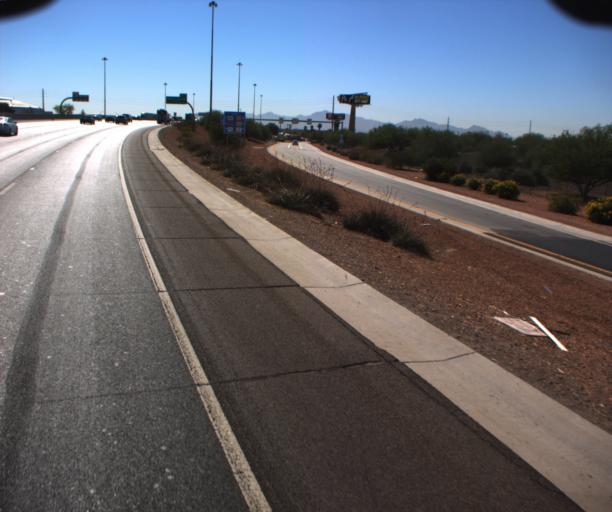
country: US
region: Arizona
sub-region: Maricopa County
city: Peoria
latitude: 33.5403
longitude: -112.2704
